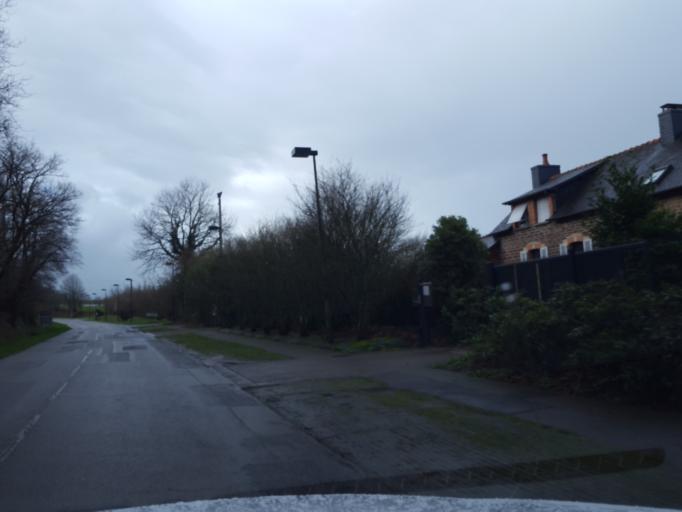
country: FR
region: Brittany
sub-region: Departement d'Ille-et-Vilaine
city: Guignen
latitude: 47.9167
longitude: -1.8611
